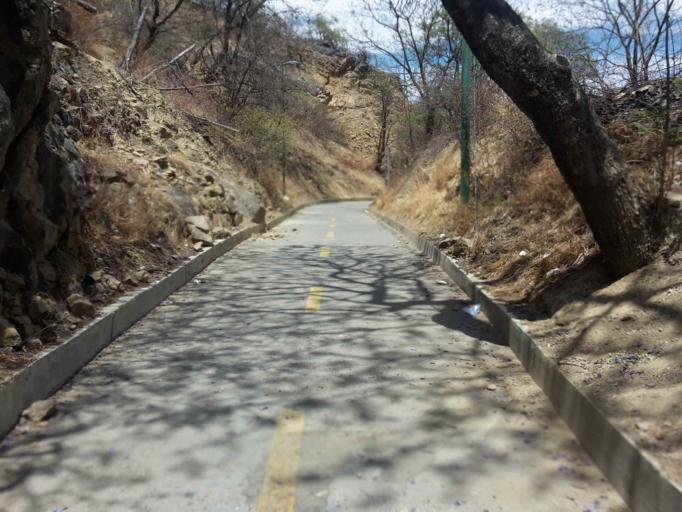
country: BO
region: Cochabamba
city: Cochabamba
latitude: -17.3774
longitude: -66.1381
